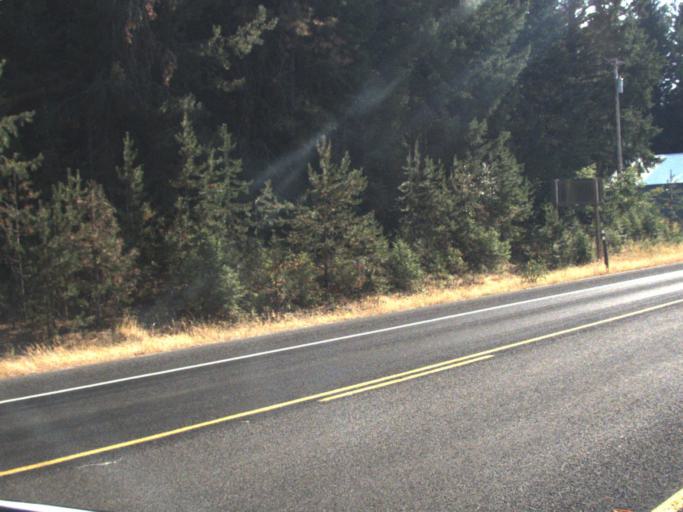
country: US
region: Washington
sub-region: Pend Oreille County
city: Newport
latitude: 48.1224
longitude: -117.1985
